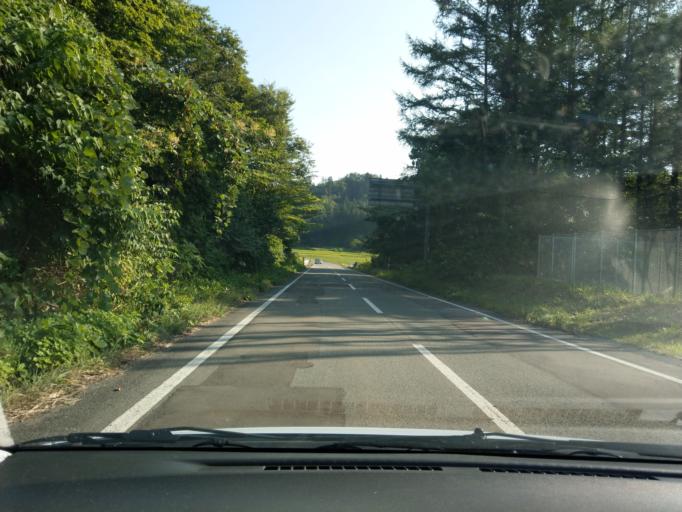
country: JP
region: Akita
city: Akita
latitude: 39.5950
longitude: 140.2334
